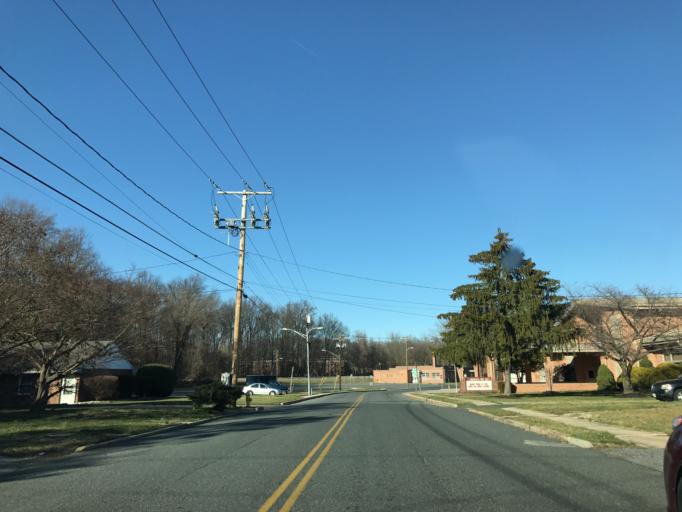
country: US
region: Maryland
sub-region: Harford County
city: Aberdeen
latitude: 39.5115
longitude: -76.1661
